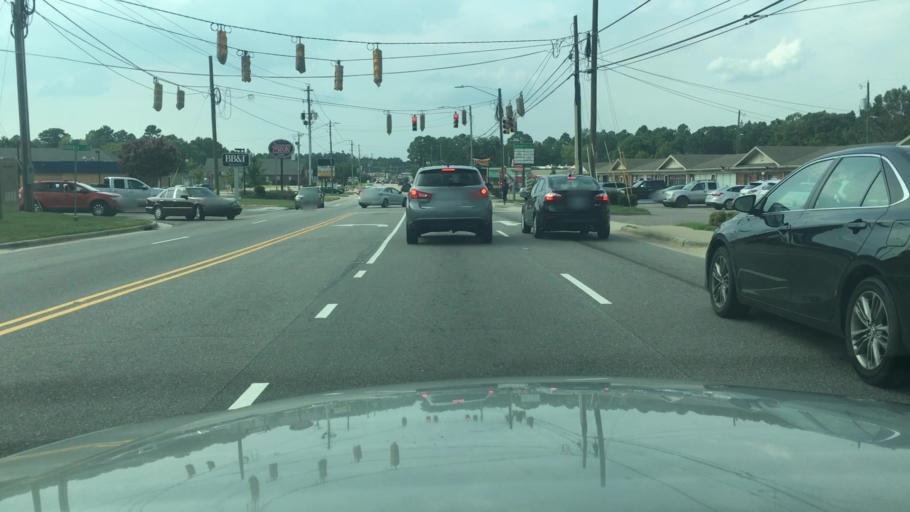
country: US
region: North Carolina
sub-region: Cumberland County
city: Fort Bragg
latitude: 35.0915
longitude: -78.9840
